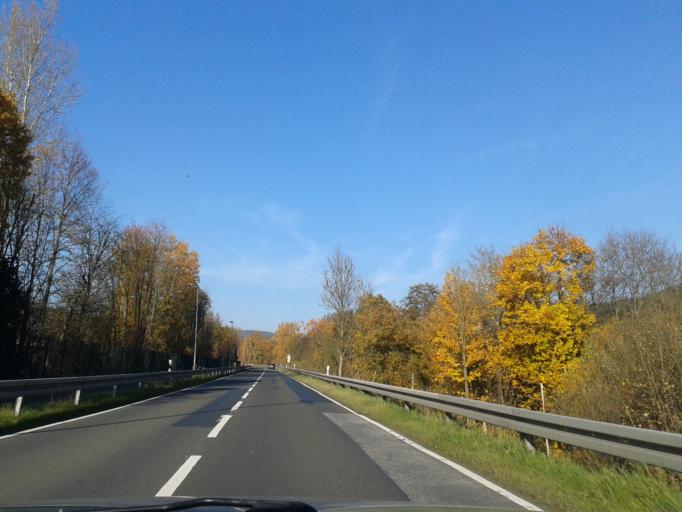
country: DE
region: Hesse
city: Dillenburg
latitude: 50.8177
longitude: 8.3376
